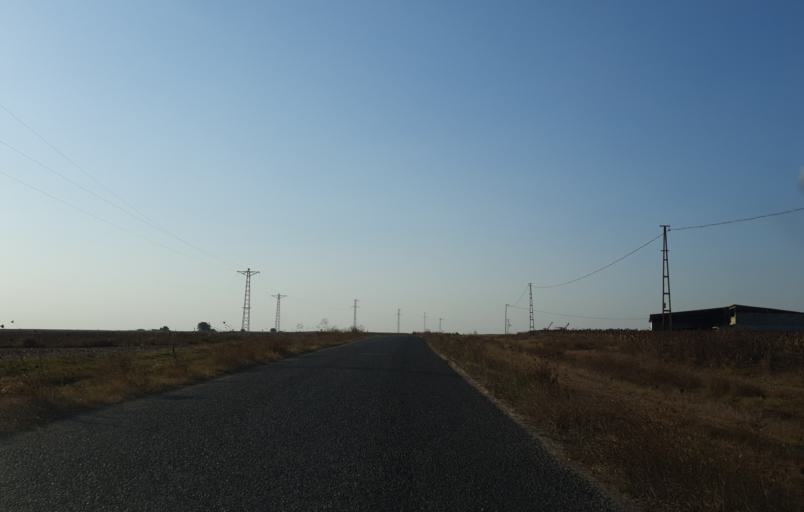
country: TR
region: Tekirdag
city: Beyazkoy
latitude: 41.3973
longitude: 27.7620
